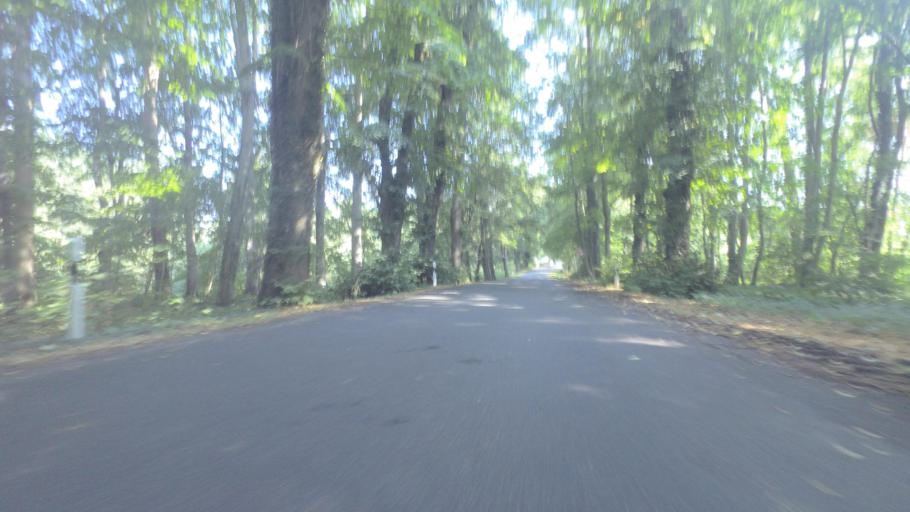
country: DE
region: Mecklenburg-Vorpommern
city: Pampow
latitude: 53.6782
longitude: 12.5564
